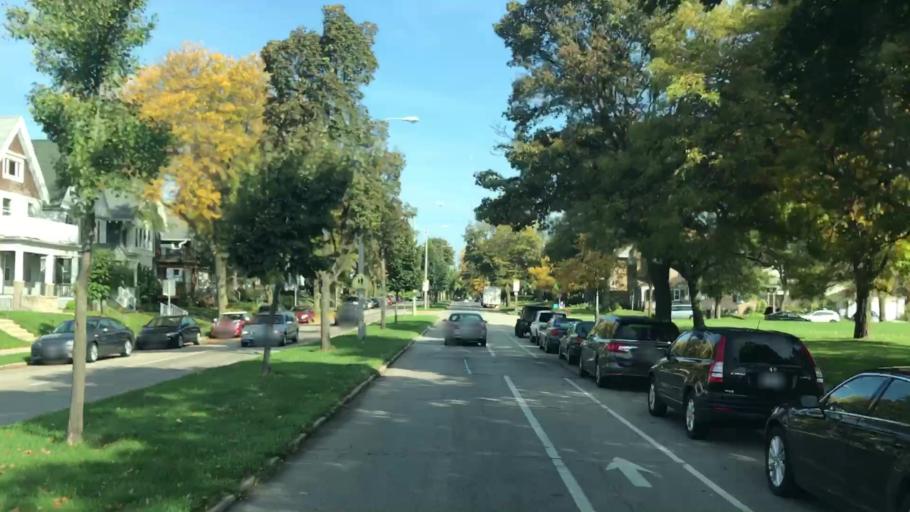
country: US
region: Wisconsin
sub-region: Milwaukee County
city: Shorewood
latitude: 43.0730
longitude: -87.8977
